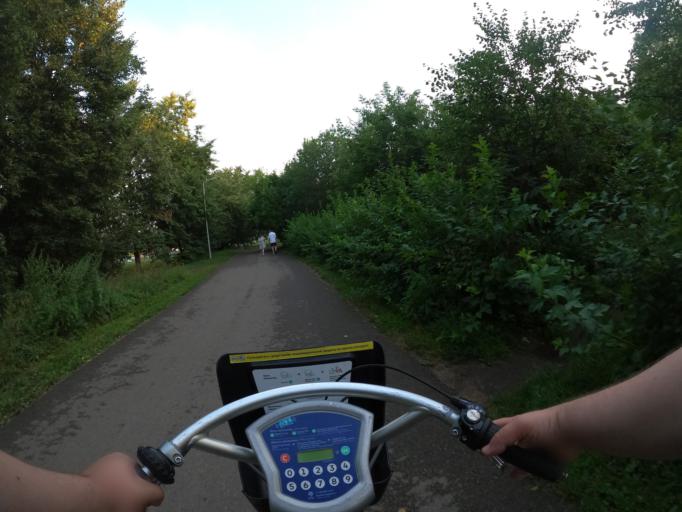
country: RU
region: Moscow
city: Strogino
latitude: 55.8070
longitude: 37.4294
